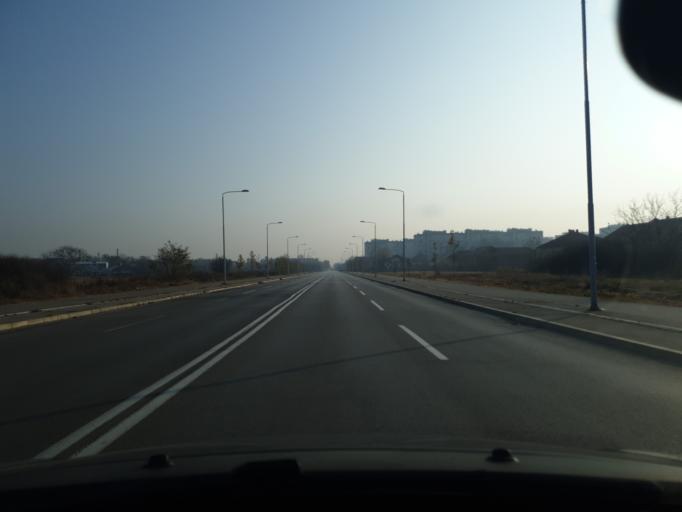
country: RS
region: Central Serbia
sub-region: Jablanicki Okrug
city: Leskovac
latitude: 43.0036
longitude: 21.9277
